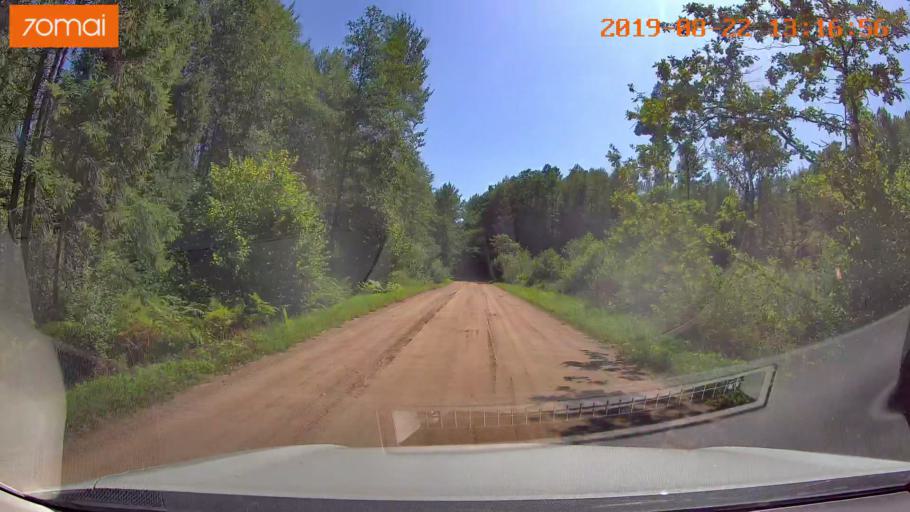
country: BY
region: Minsk
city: Prawdzinski
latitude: 53.2519
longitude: 27.9163
